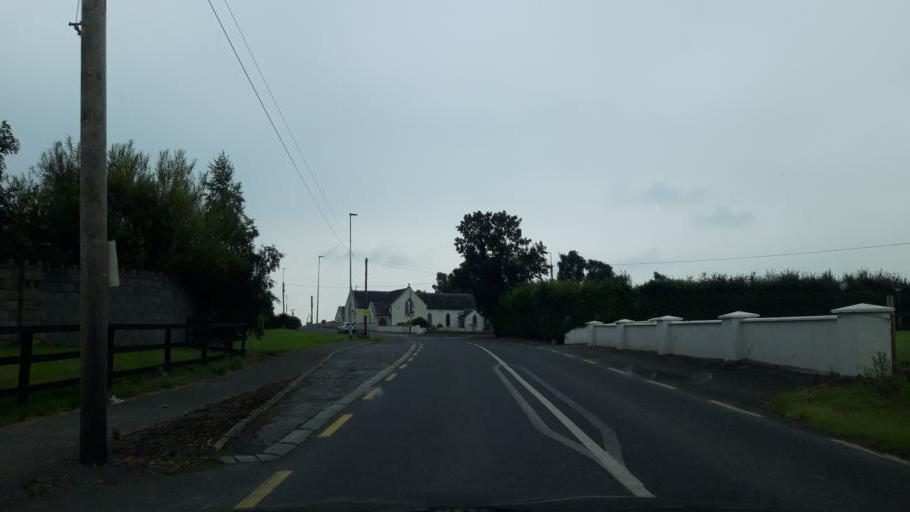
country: IE
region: Munster
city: Fethard
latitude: 52.4191
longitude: -7.7033
